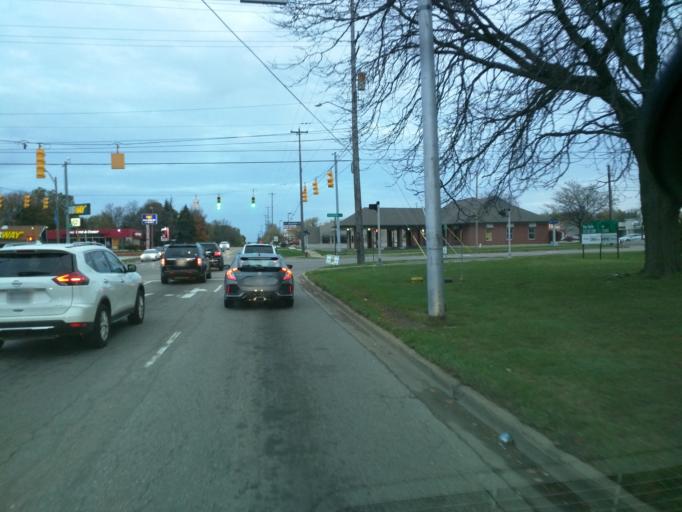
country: US
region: Michigan
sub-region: Ingham County
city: Edgemont Park
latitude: 42.7406
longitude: -84.6029
